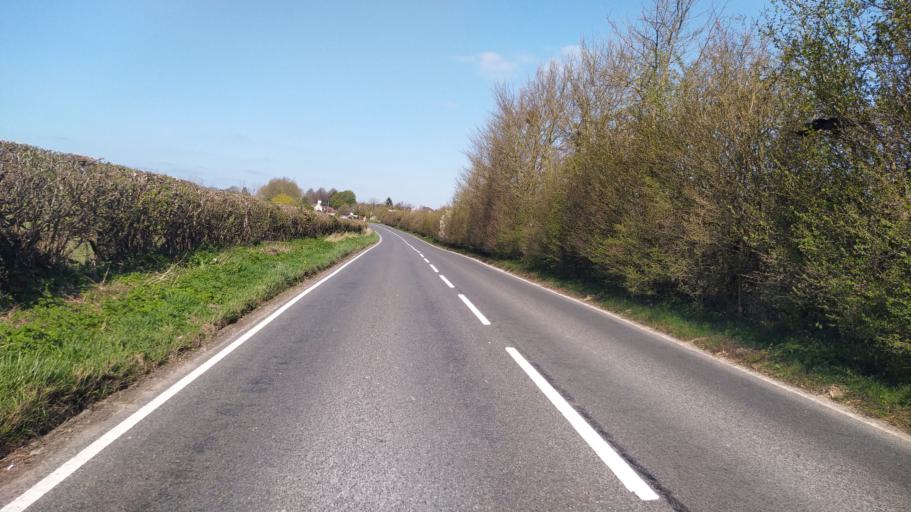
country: GB
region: England
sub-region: Dorset
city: Lytchett Matravers
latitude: 50.7951
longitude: -2.0803
